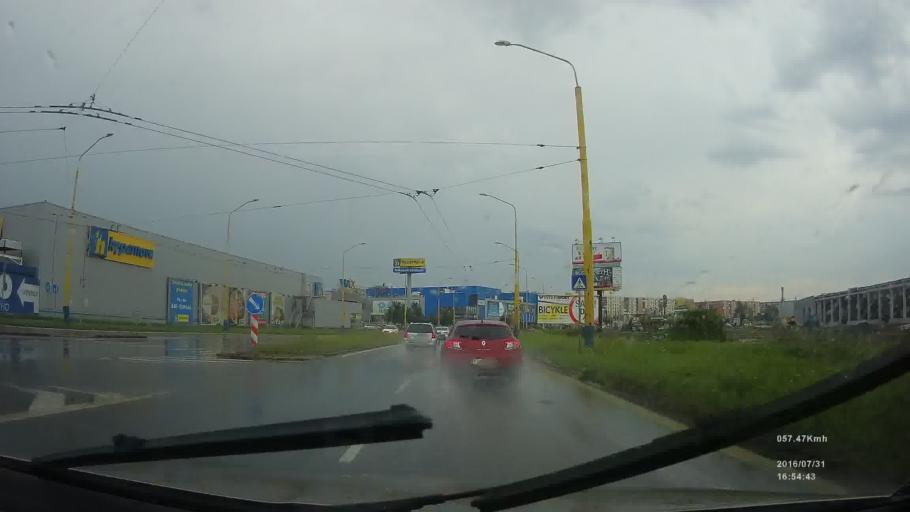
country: SK
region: Presovsky
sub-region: Okres Presov
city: Presov
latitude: 49.0005
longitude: 21.2692
